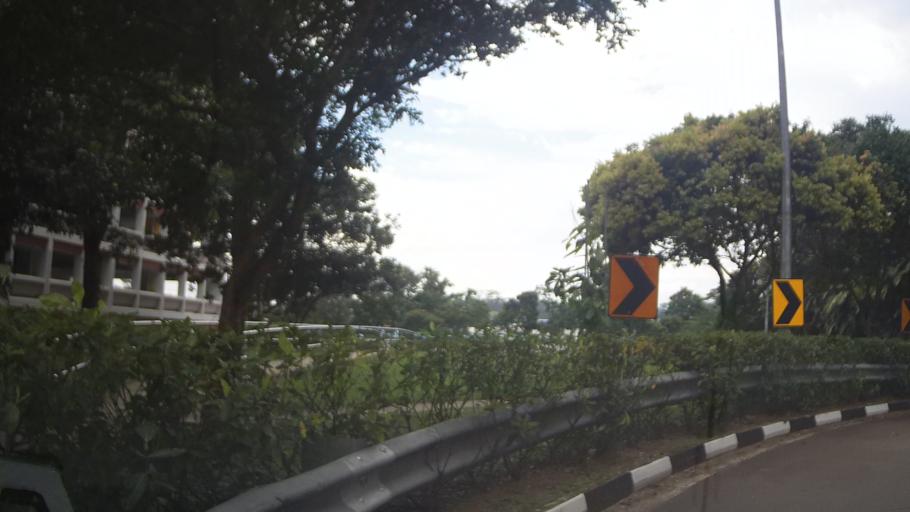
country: MY
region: Johor
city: Johor Bahru
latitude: 1.3997
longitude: 103.7512
